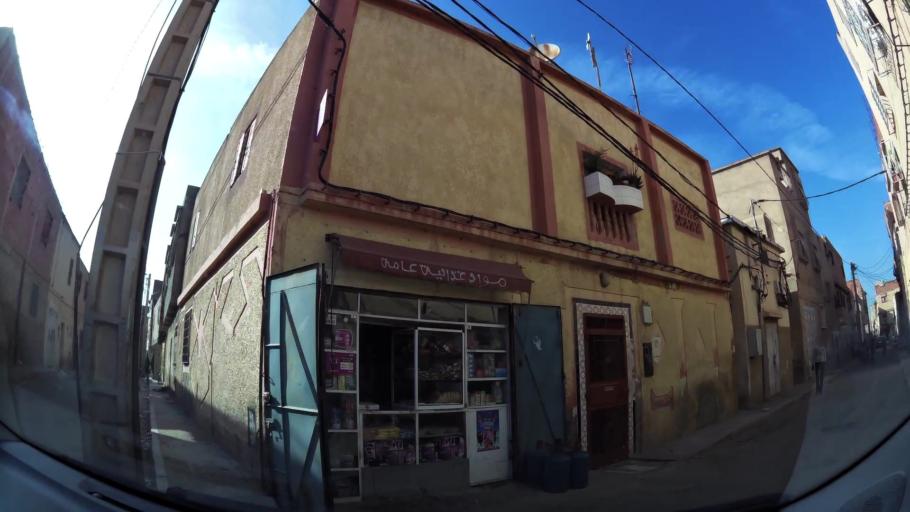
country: MA
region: Oriental
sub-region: Oujda-Angad
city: Oujda
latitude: 34.7128
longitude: -1.8904
